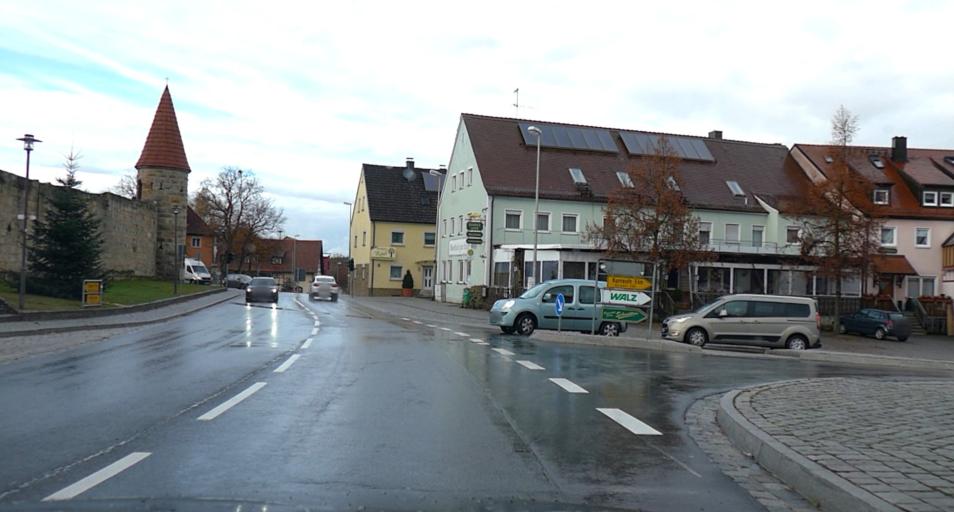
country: DE
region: Bavaria
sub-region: Upper Franconia
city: Effeltrich
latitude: 49.6595
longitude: 11.0927
